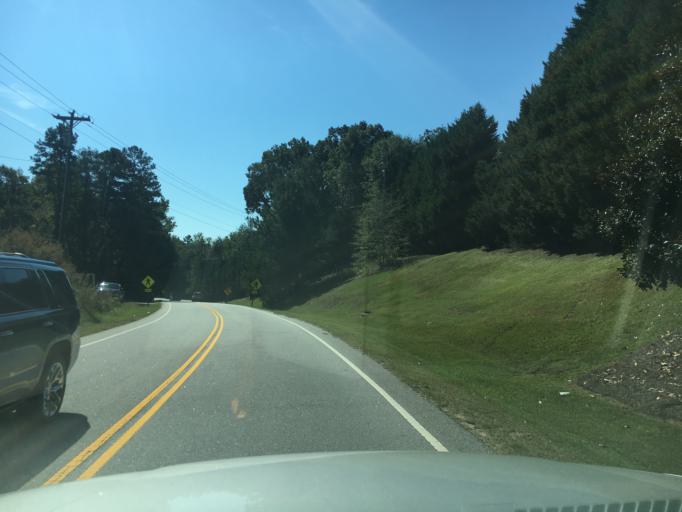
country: US
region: South Carolina
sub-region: Greenville County
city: Taylors
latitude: 34.8871
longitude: -82.2850
